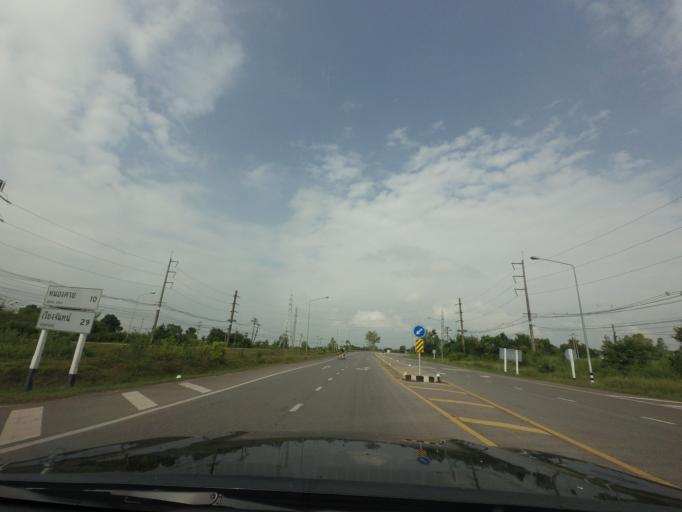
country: TH
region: Nong Khai
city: Nong Khai
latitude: 17.8127
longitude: 102.7552
